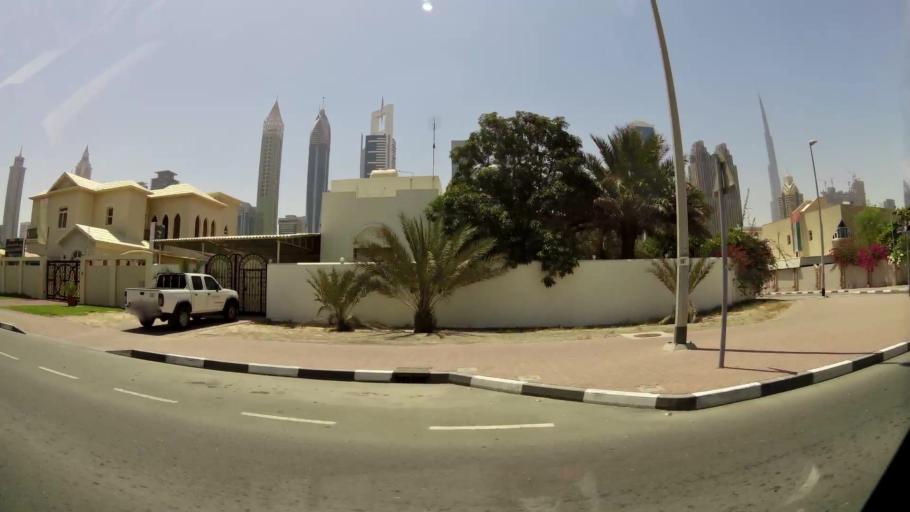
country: AE
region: Dubai
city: Dubai
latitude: 25.2134
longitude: 55.2694
